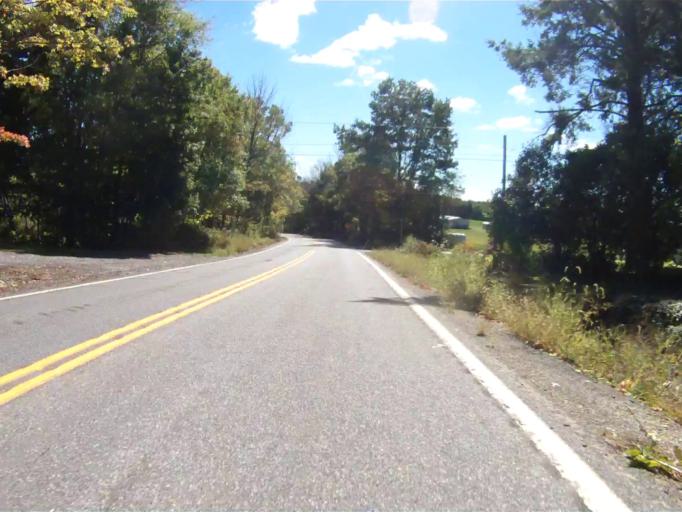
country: US
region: Pennsylvania
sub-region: Centre County
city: Park Forest Village
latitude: 40.9287
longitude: -77.9264
